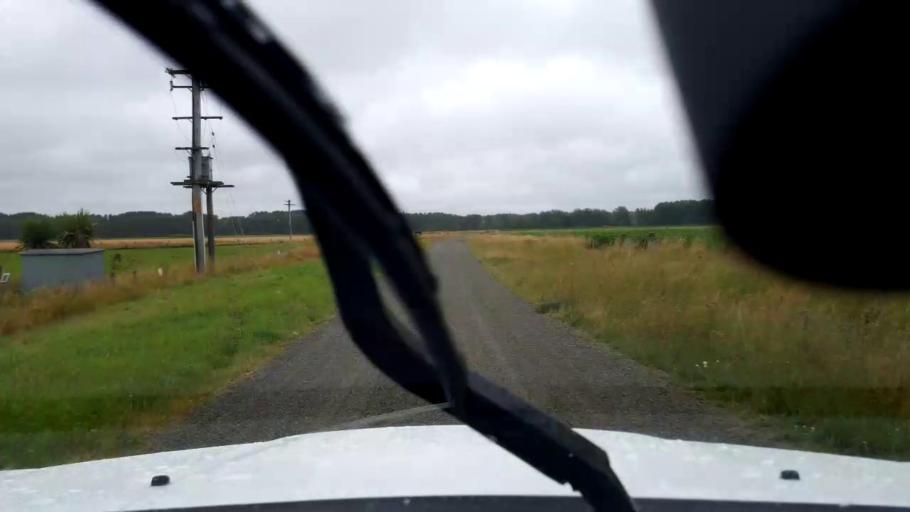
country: NZ
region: Canterbury
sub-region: Timaru District
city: Pleasant Point
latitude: -44.2520
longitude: 171.2003
